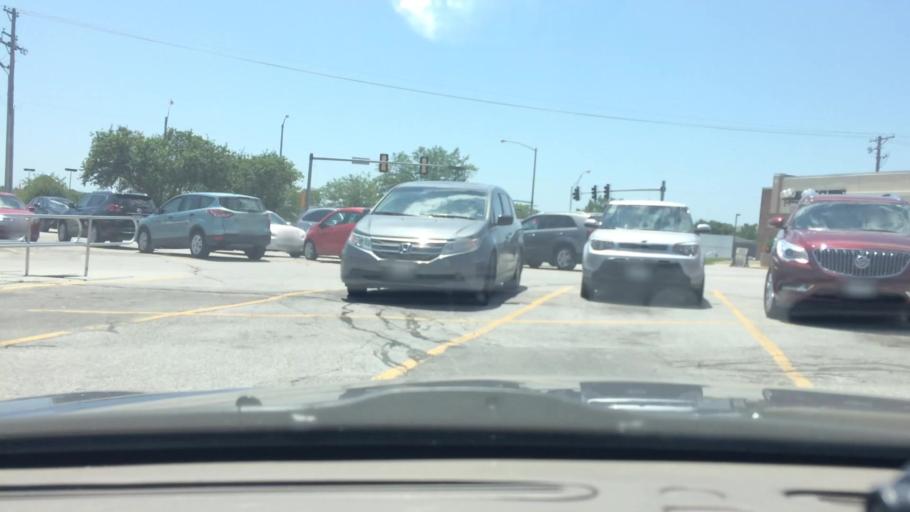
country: US
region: Nebraska
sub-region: Sarpy County
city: La Vista
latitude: 41.1769
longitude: -96.0452
